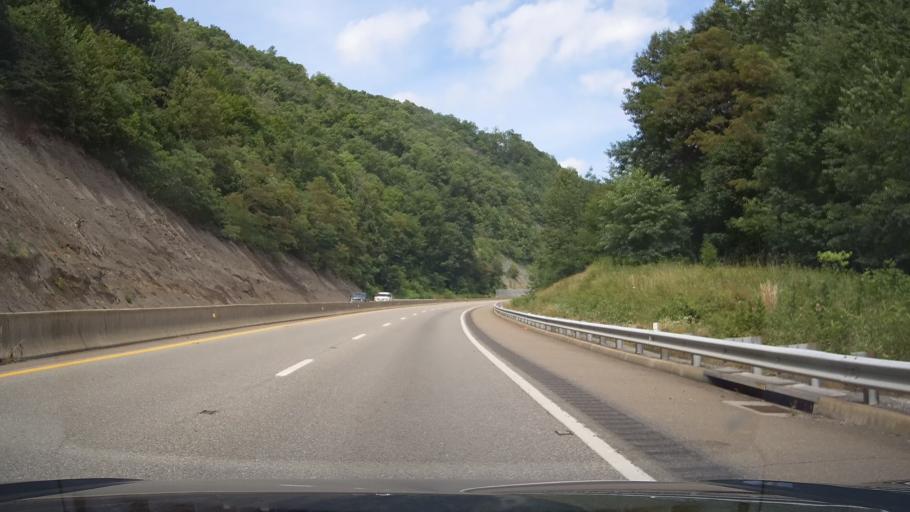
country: US
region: Virginia
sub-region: City of Norton
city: Norton
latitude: 36.9088
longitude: -82.6828
